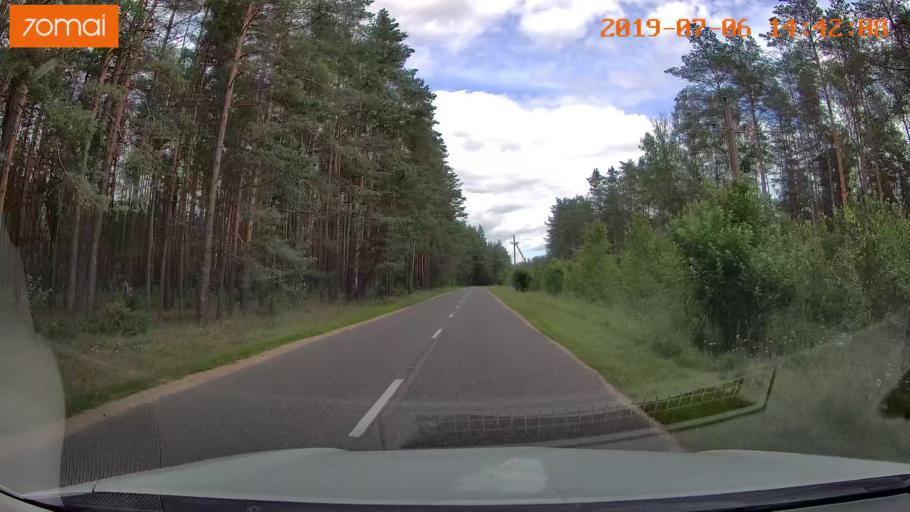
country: BY
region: Minsk
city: Ivyanyets
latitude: 53.9386
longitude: 26.6850
